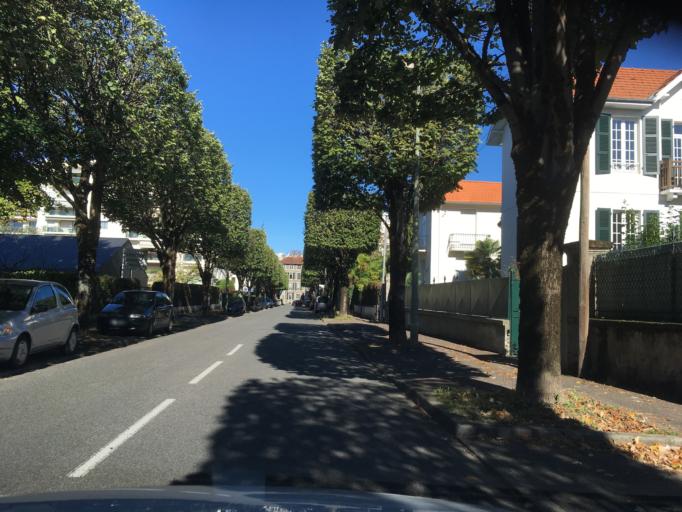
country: FR
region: Aquitaine
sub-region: Departement des Pyrenees-Atlantiques
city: Pau
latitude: 43.3001
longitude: -0.3556
